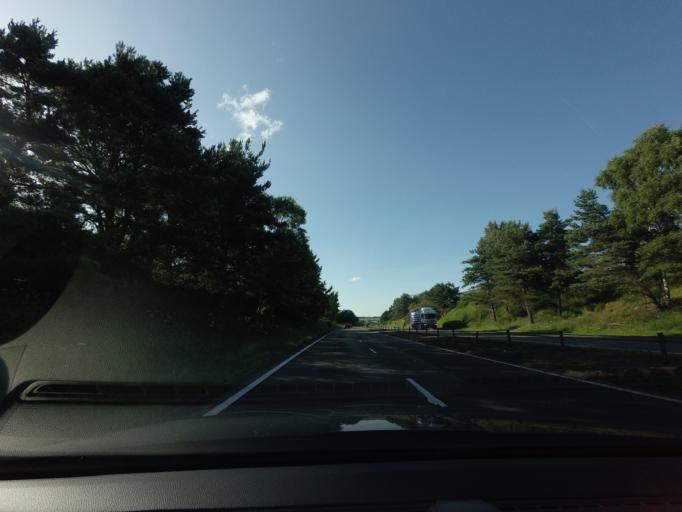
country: GB
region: Scotland
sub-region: Highland
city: Inverness
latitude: 57.5291
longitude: -4.3258
